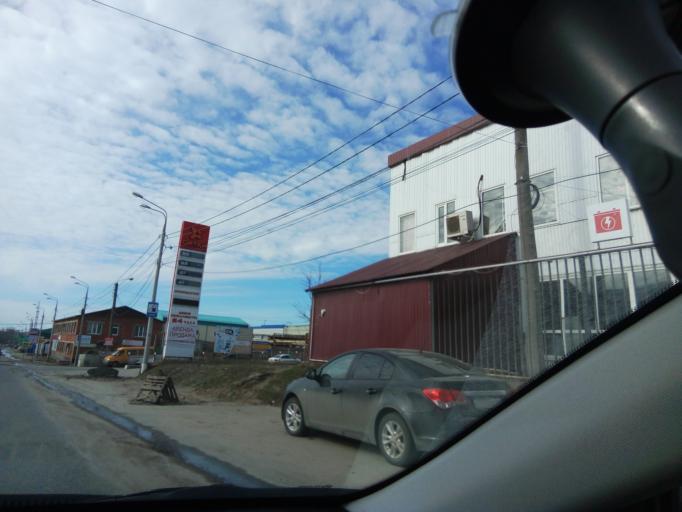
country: RU
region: Chuvashia
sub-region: Cheboksarskiy Rayon
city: Cheboksary
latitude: 56.1056
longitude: 47.2501
